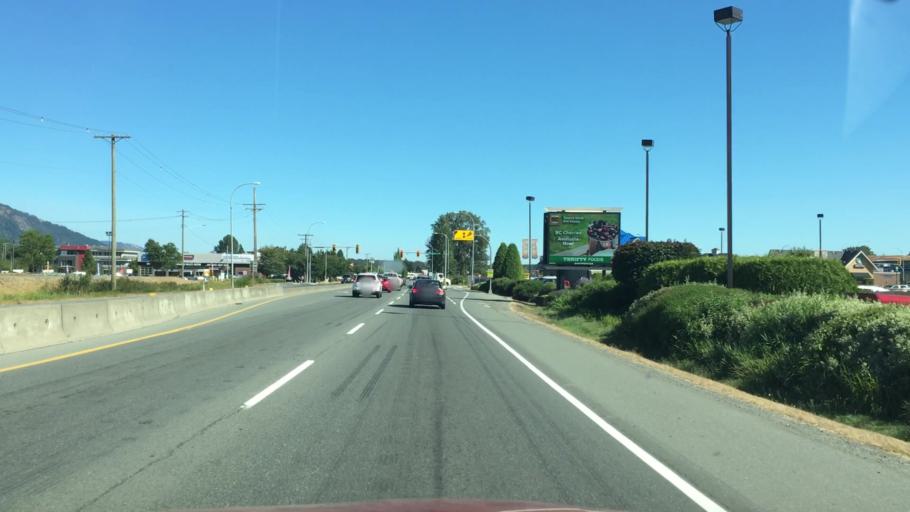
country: CA
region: British Columbia
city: Duncan
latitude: 48.7876
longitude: -123.7081
